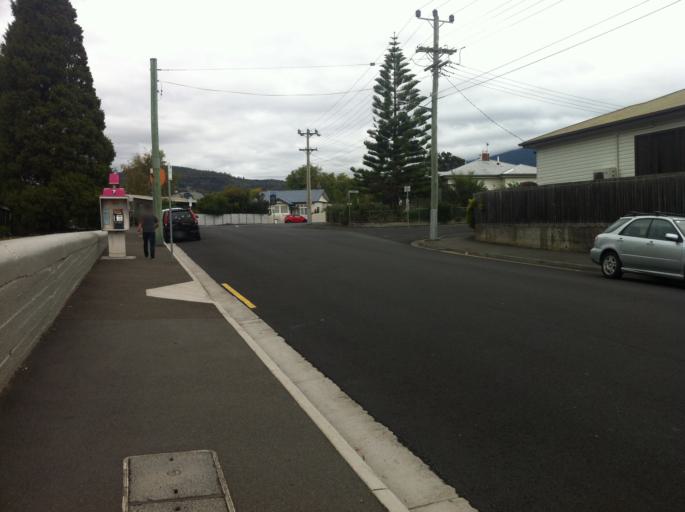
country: AU
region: Tasmania
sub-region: Glenorchy
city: Moonah
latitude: -42.8516
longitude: 147.3058
